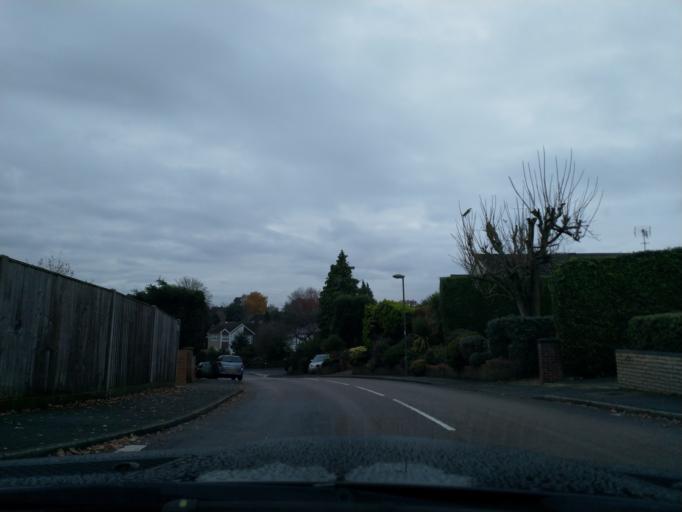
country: GB
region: England
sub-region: Surrey
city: Frimley
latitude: 51.3170
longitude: -0.7319
